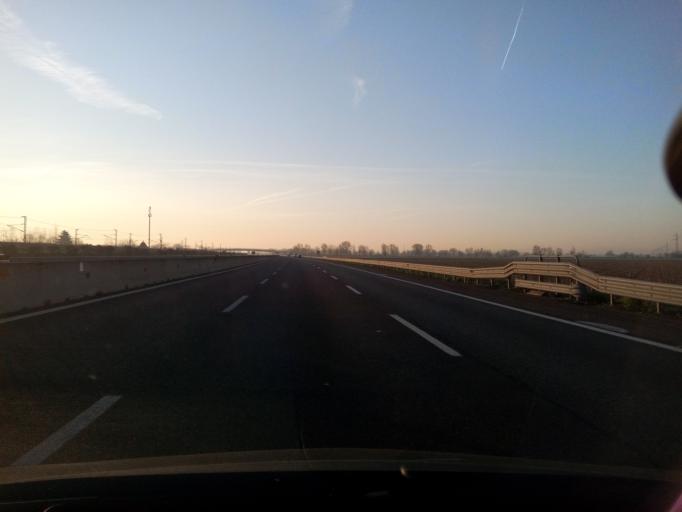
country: IT
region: Lombardy
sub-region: Provincia di Lodi
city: Lodi Vecchio
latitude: 45.2995
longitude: 9.4089
